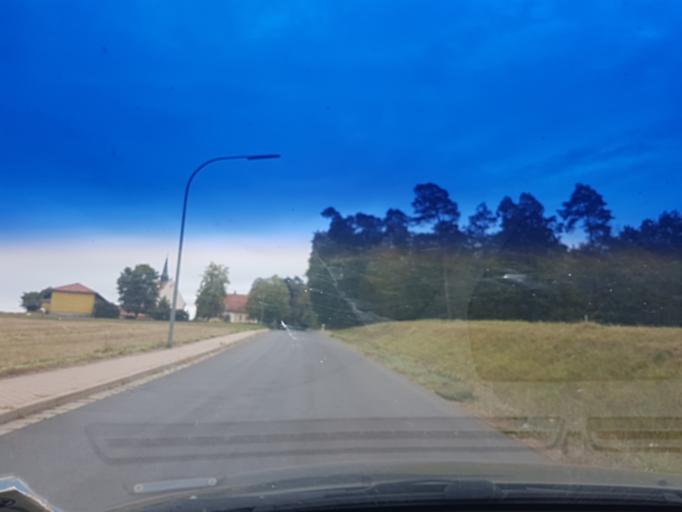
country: DE
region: Bavaria
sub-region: Regierungsbezirk Unterfranken
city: Geiselwind
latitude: 49.8275
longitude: 10.4839
